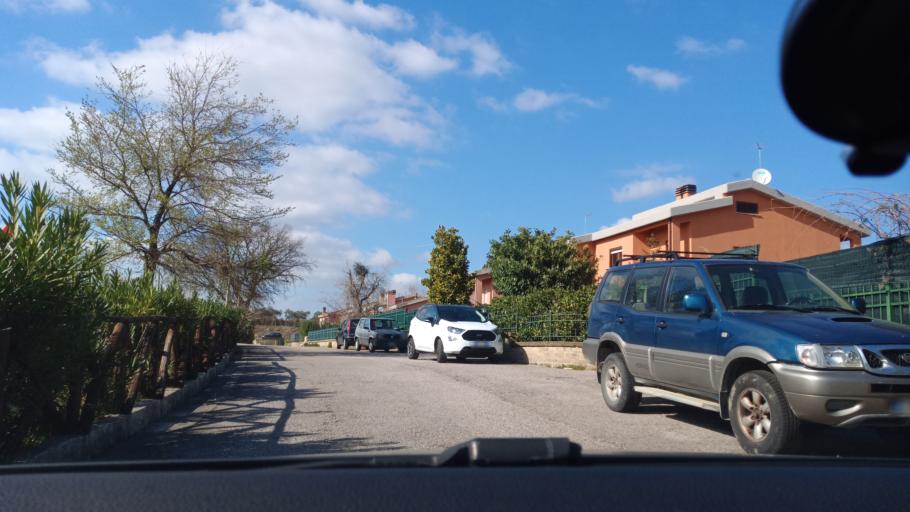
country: IT
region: Latium
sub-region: Citta metropolitana di Roma Capitale
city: Torrita Tiberina
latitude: 42.2453
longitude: 12.6145
